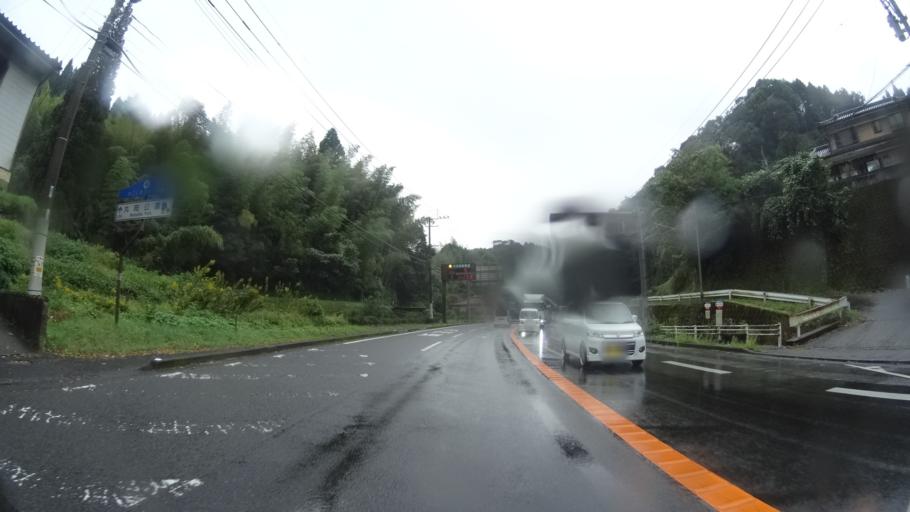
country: JP
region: Kagoshima
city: Kajiki
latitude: 31.9006
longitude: 130.7001
